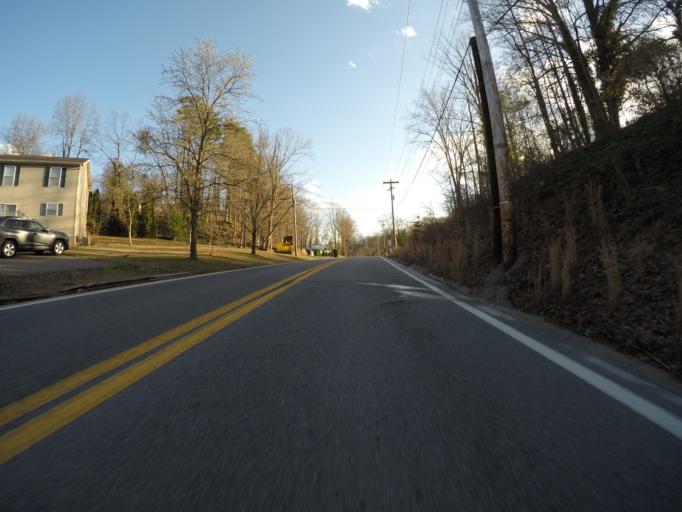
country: US
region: West Virginia
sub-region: Kanawha County
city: Charleston
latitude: 38.3898
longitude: -81.5929
